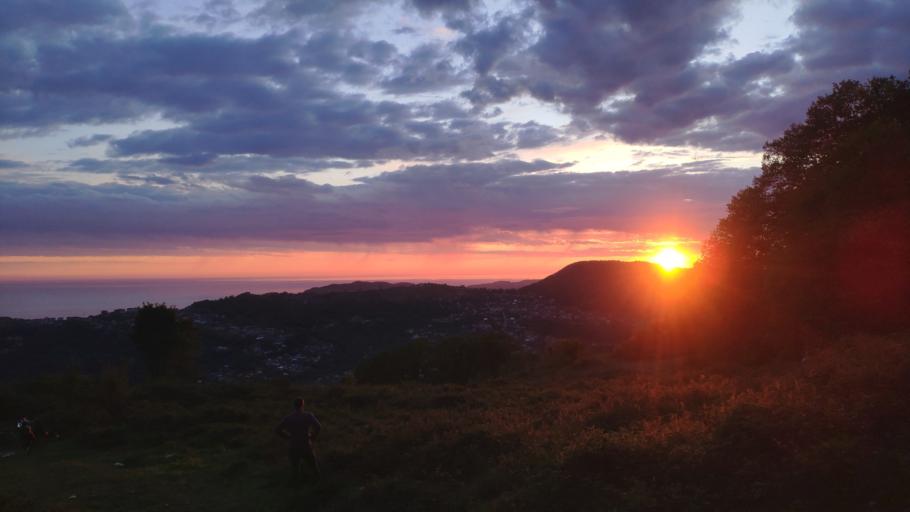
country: RU
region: Krasnodarskiy
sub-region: Sochi City
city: Sochi
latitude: 43.6463
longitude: 39.7734
